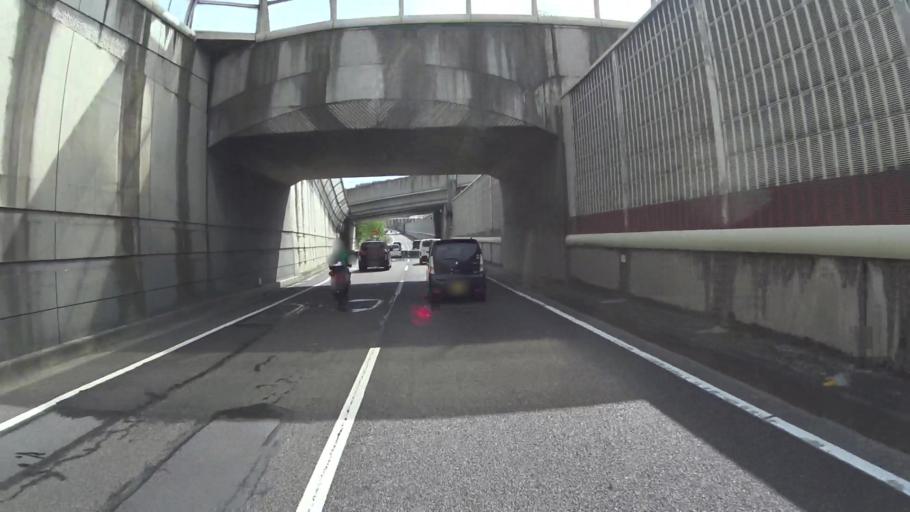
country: JP
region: Shiga Prefecture
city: Otsu-shi
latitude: 35.0503
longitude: 135.8617
